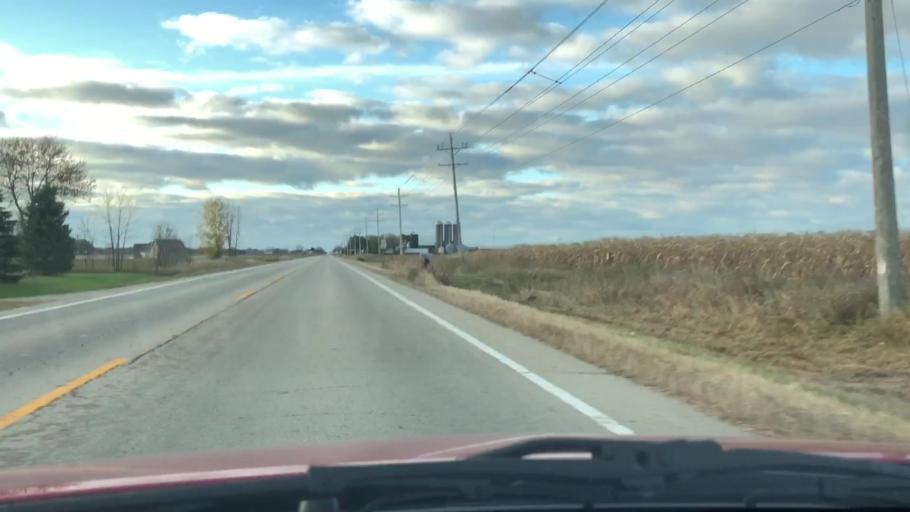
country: US
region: Wisconsin
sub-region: Outagamie County
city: Seymour
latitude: 44.4475
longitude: -88.2913
